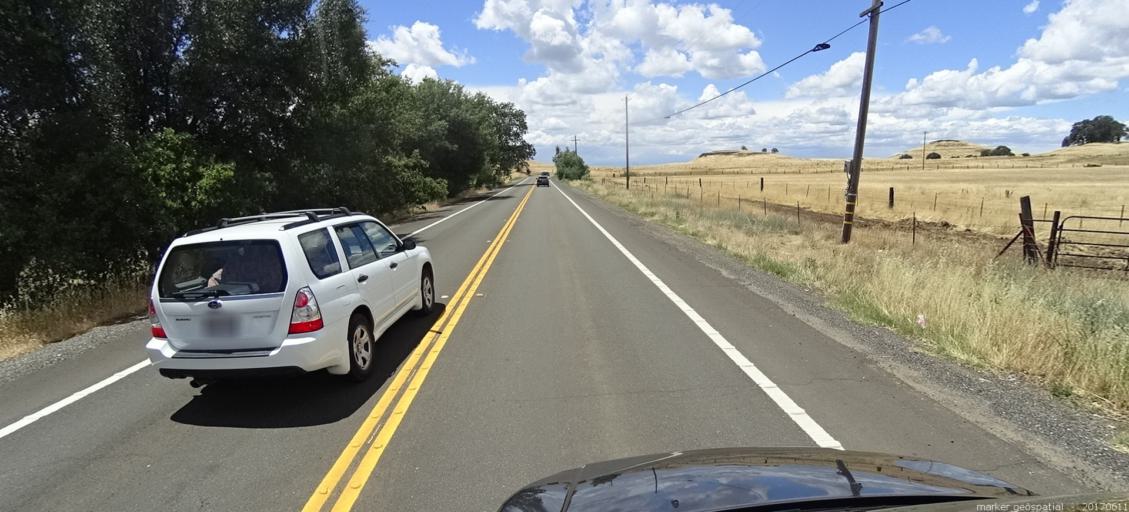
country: US
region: California
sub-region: Butte County
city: Paradise
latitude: 39.6401
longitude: -121.6636
